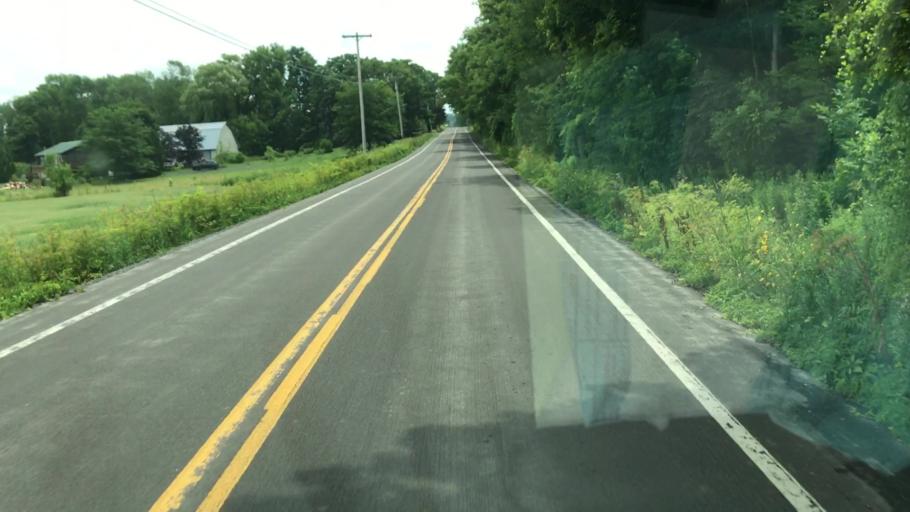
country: US
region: New York
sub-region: Onondaga County
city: Manlius
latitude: 42.9341
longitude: -75.9768
